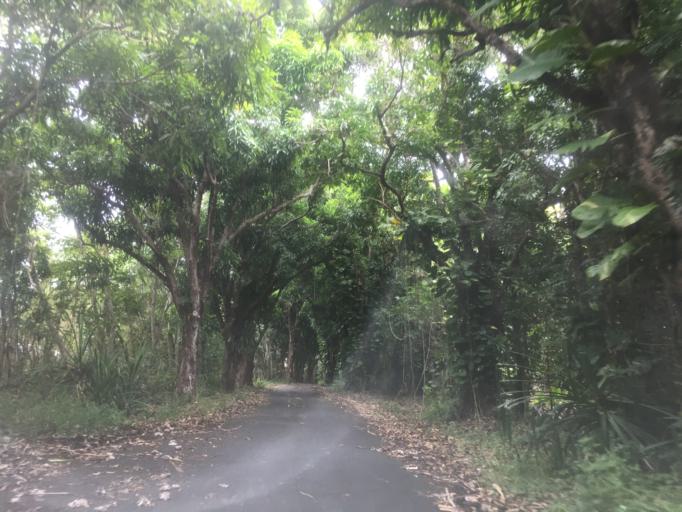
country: US
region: Hawaii
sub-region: Hawaii County
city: Leilani Estates
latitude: 19.4652
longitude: -154.8544
